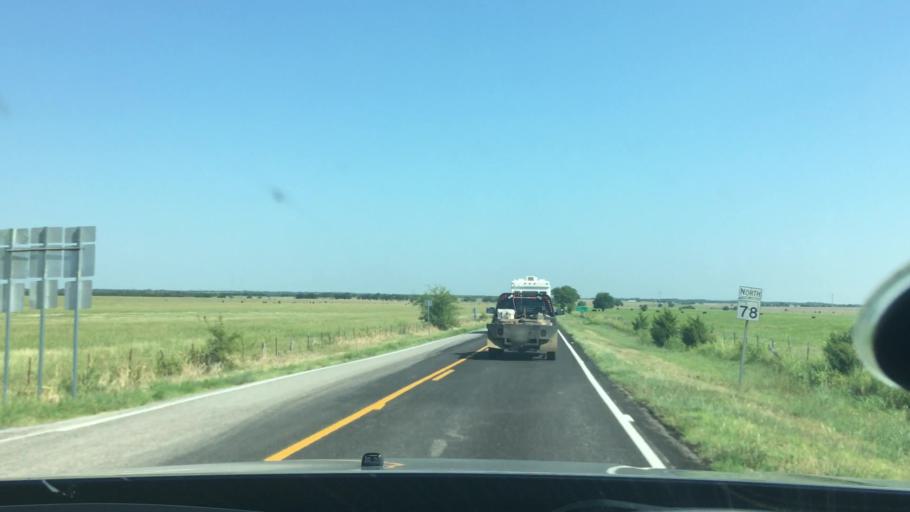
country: US
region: Oklahoma
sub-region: Johnston County
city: Tishomingo
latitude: 34.1448
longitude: -96.5042
